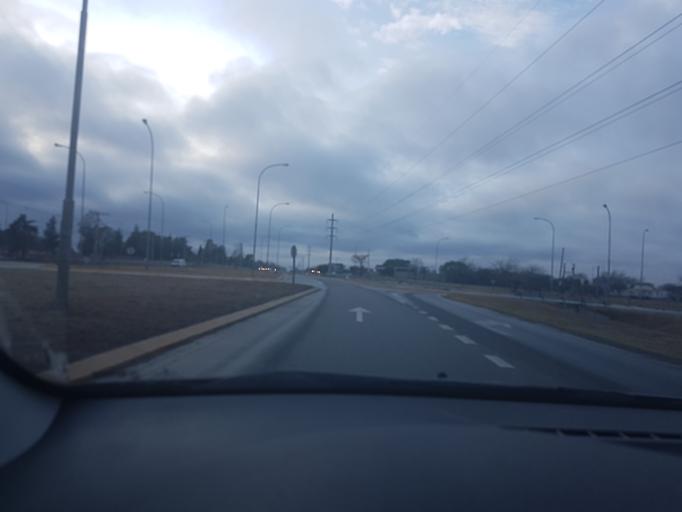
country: AR
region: Cordoba
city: Villa Allende
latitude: -31.3015
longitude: -64.2650
